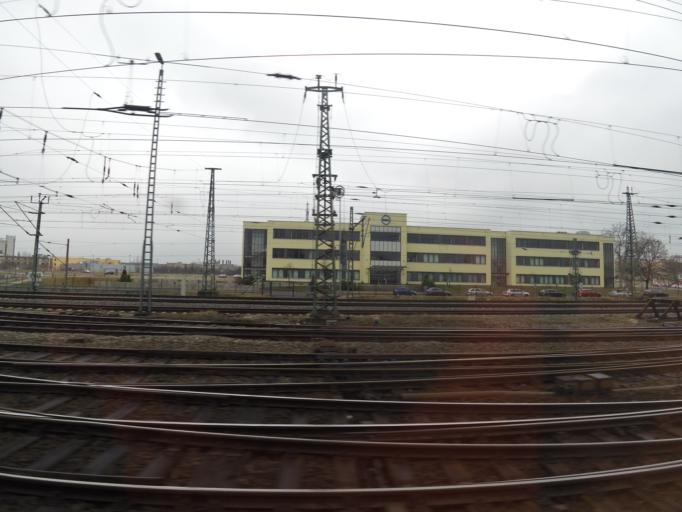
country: DE
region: Saxony-Anhalt
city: Halle (Saale)
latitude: 51.4726
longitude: 11.9922
